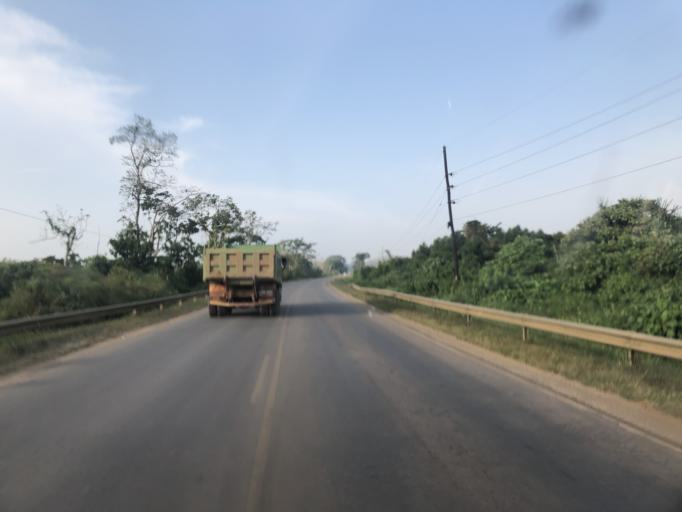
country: UG
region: Central Region
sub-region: Butambala District
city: Gombe
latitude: 0.0926
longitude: 32.1483
